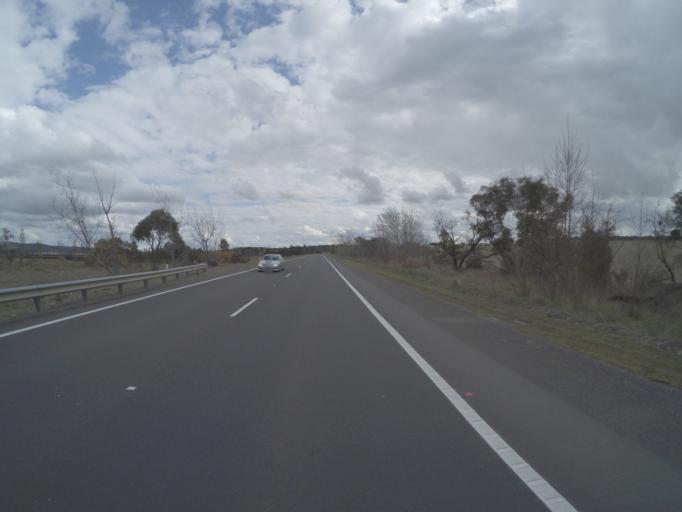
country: AU
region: New South Wales
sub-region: Goulburn Mulwaree
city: Goulburn
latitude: -34.8020
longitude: 149.6094
